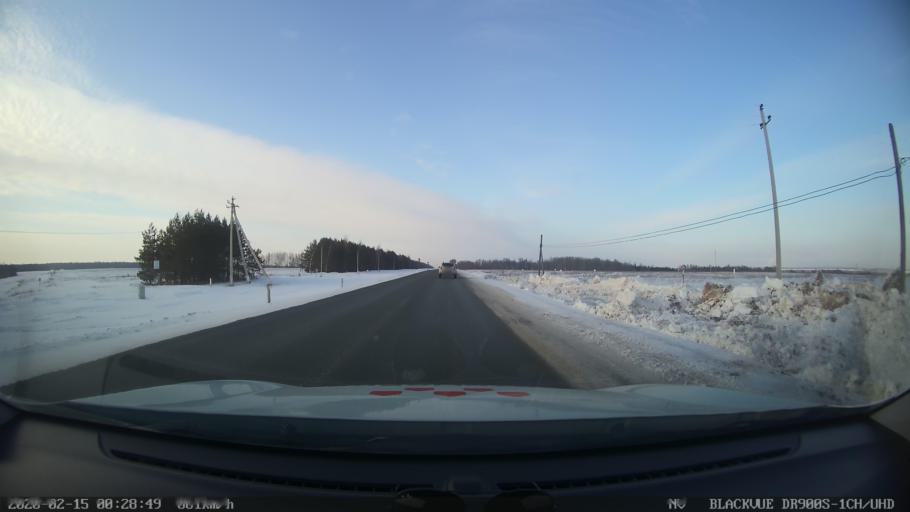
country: RU
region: Tatarstan
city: Verkhniy Uslon
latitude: 55.6454
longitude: 48.8736
